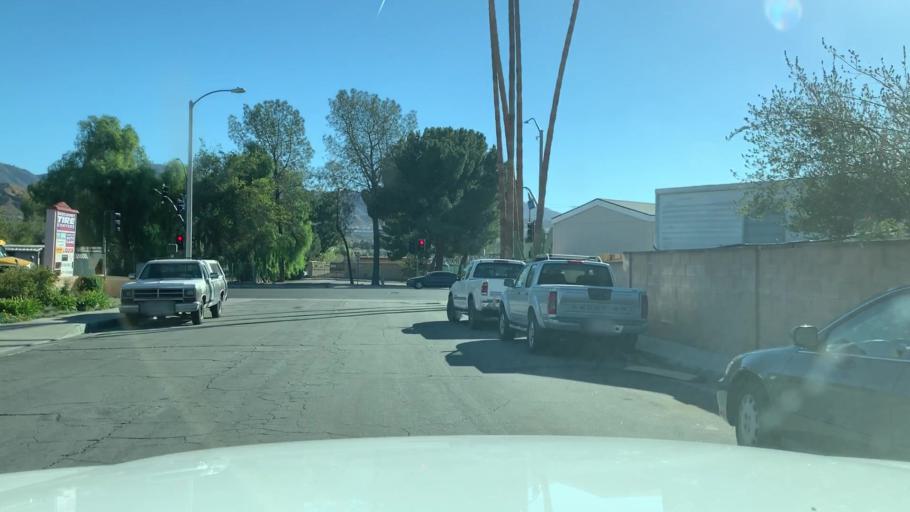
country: US
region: California
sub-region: Los Angeles County
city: Santa Clarita
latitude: 34.4170
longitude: -118.4524
